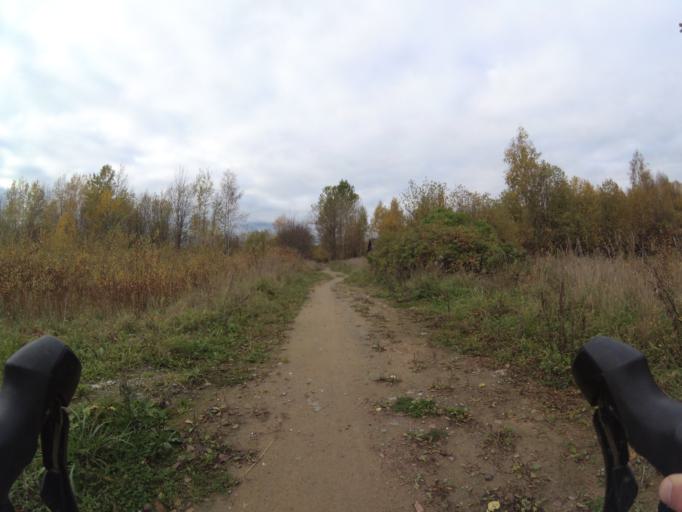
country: RU
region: St.-Petersburg
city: Lakhtinskiy
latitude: 60.0059
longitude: 30.1474
